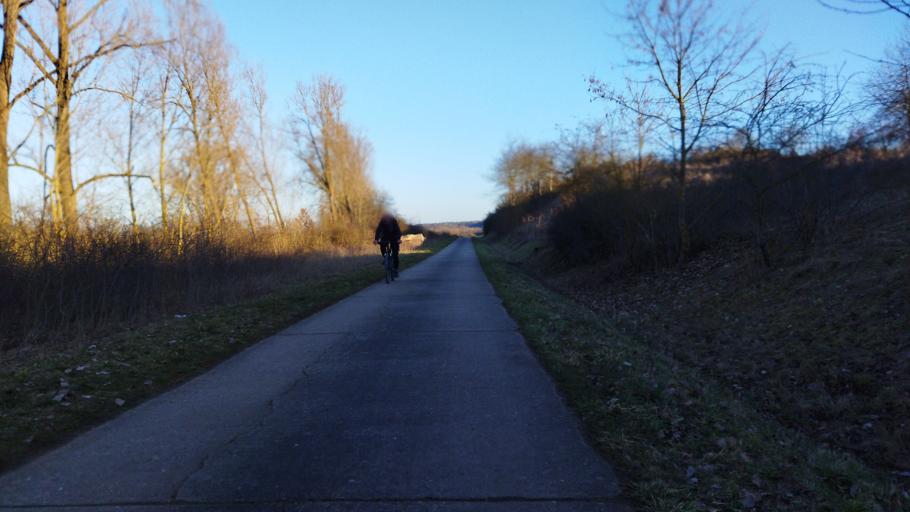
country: DE
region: Bavaria
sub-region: Regierungsbezirk Unterfranken
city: Dettelbach
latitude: 49.7925
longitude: 10.1818
